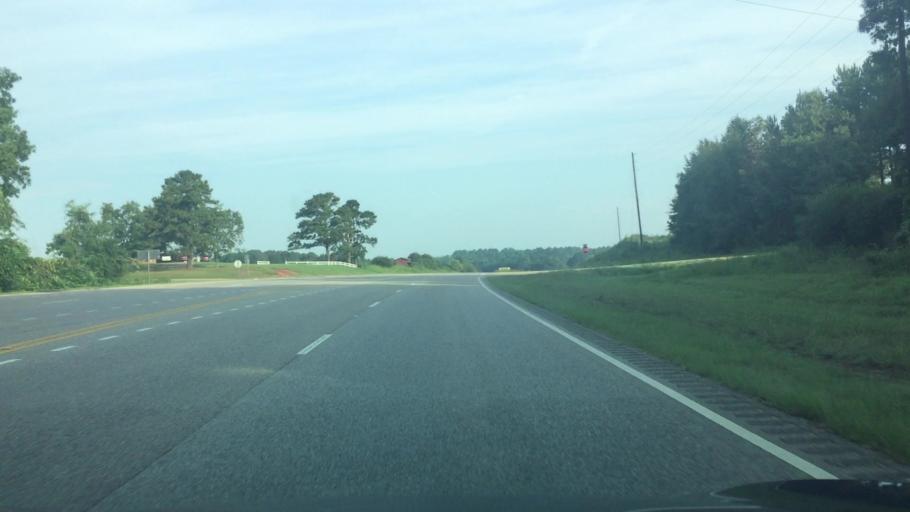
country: US
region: Alabama
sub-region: Covington County
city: Andalusia
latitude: 31.4075
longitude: -86.6026
